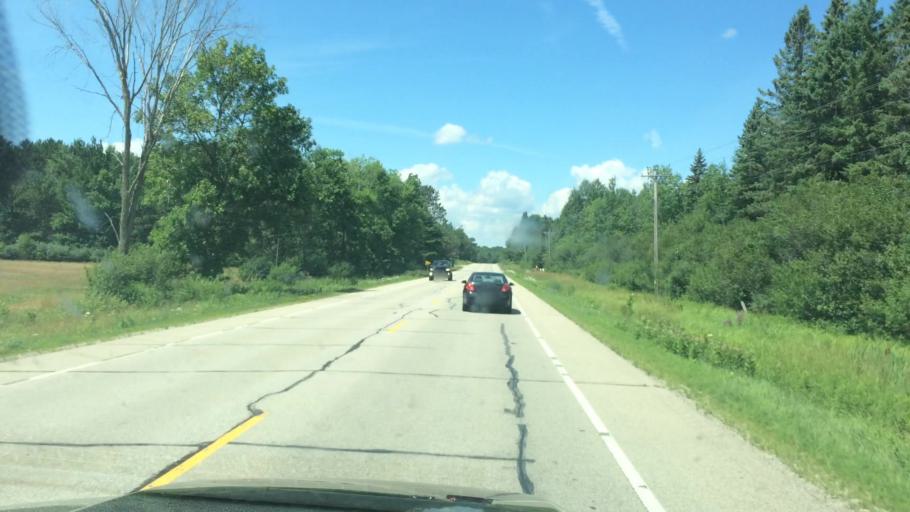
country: US
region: Wisconsin
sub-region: Marinette County
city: Peshtigo
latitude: 45.1002
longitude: -87.7297
